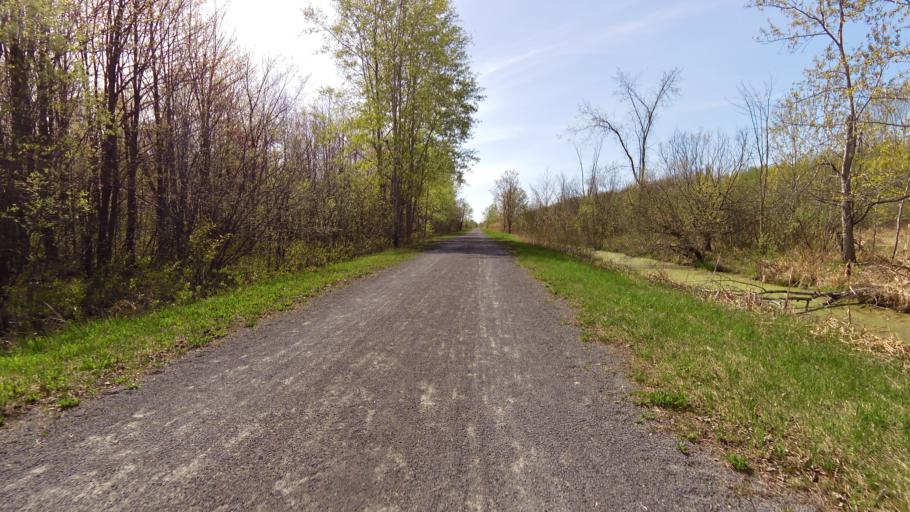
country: CA
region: Ontario
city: Clarence-Rockland
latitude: 45.4167
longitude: -75.4520
